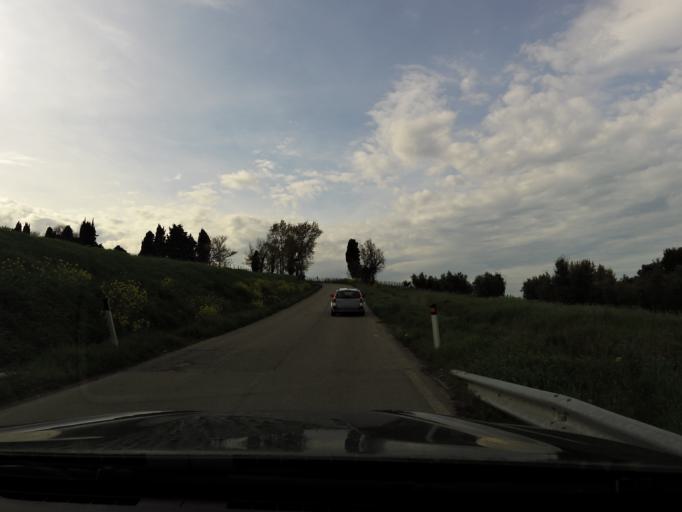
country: IT
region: The Marches
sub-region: Provincia di Macerata
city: Porto Potenza Picena
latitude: 43.3562
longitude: 13.6921
